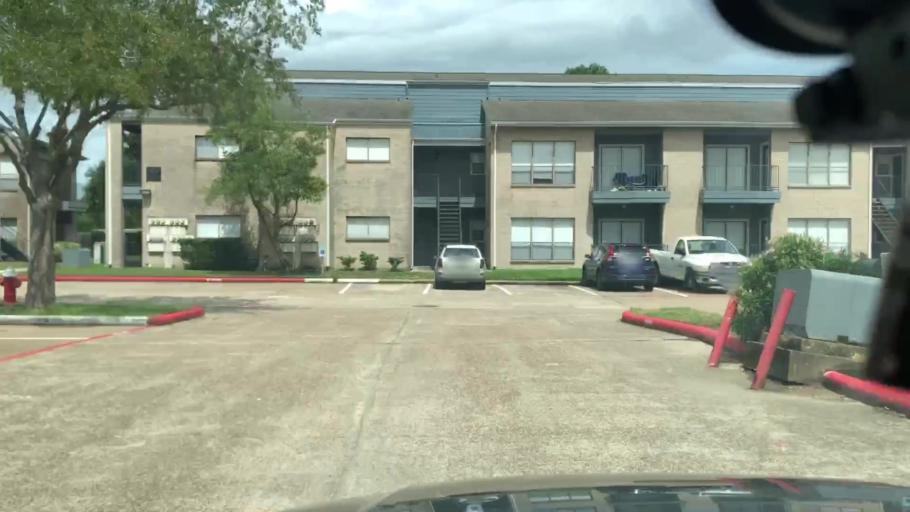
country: US
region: Texas
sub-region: Harris County
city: Nassau Bay
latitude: 29.5364
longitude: -95.1006
